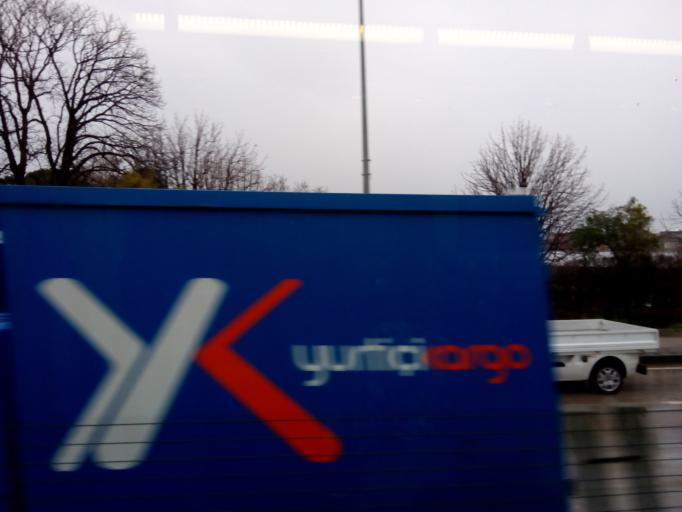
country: TR
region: Bursa
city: Yildirim
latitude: 40.2101
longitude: 29.0247
